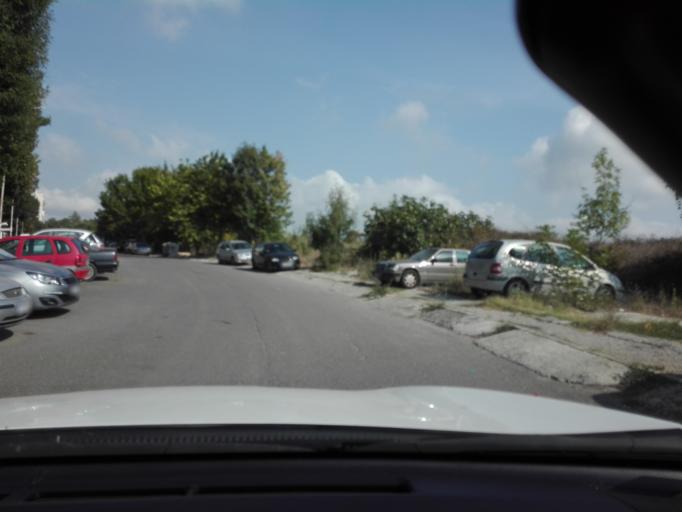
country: BG
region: Burgas
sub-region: Obshtina Burgas
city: Burgas
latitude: 42.4522
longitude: 27.4251
